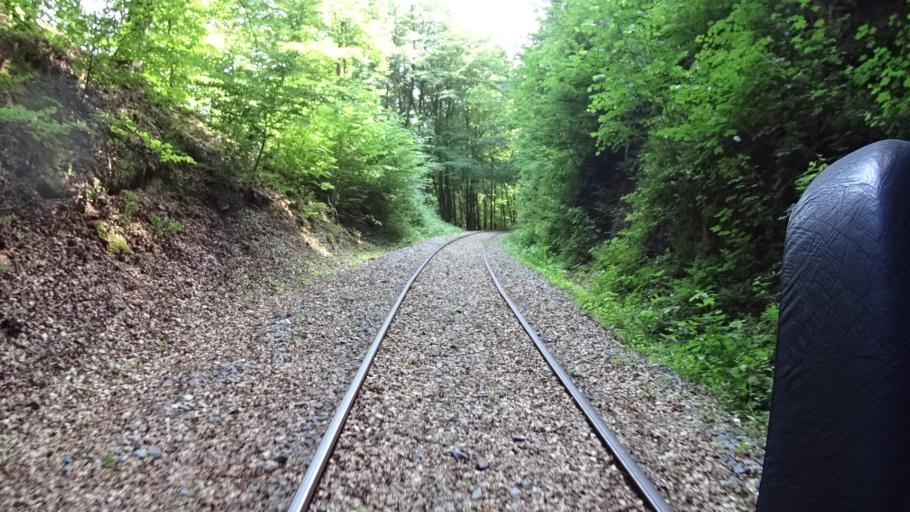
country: DE
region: Hesse
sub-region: Regierungsbezirk Darmstadt
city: Morlenbach
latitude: 49.5817
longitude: 8.7673
